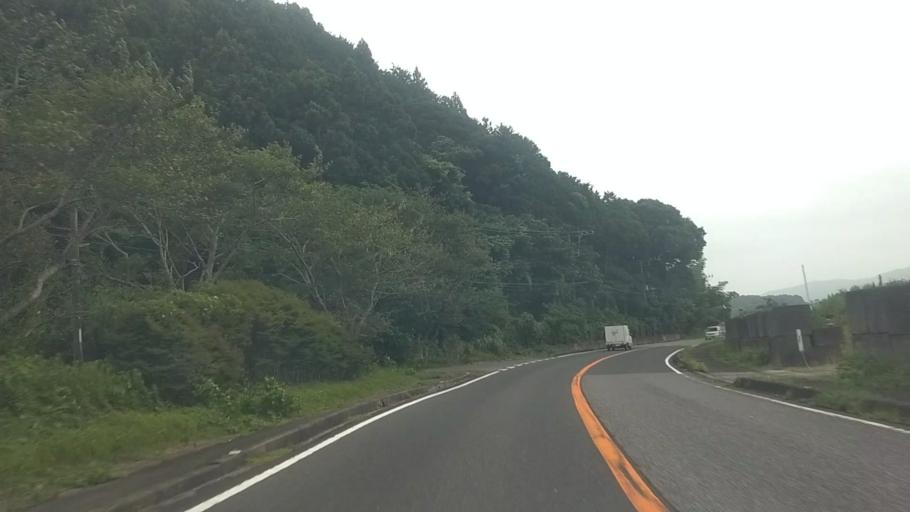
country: JP
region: Chiba
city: Kawaguchi
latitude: 35.1400
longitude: 140.0700
